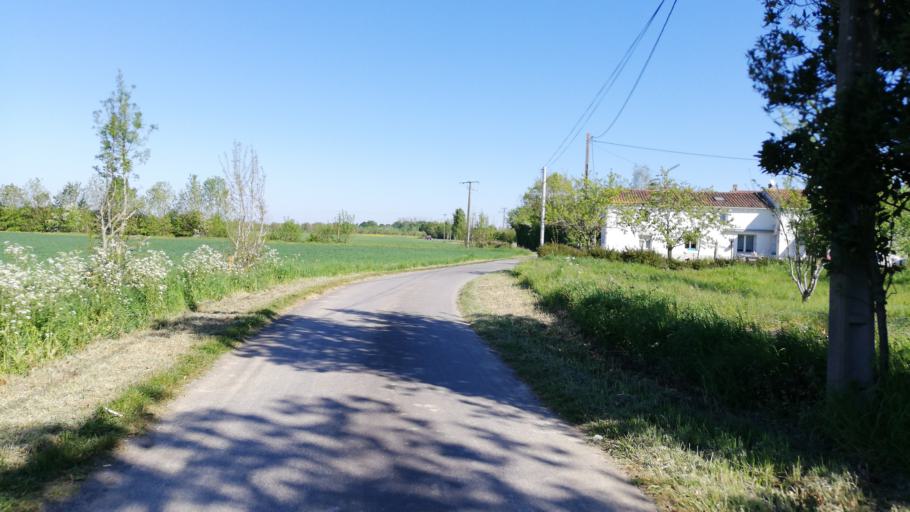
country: FR
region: Pays de la Loire
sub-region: Departement de la Vendee
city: Maillezais
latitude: 46.3288
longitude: -0.7502
